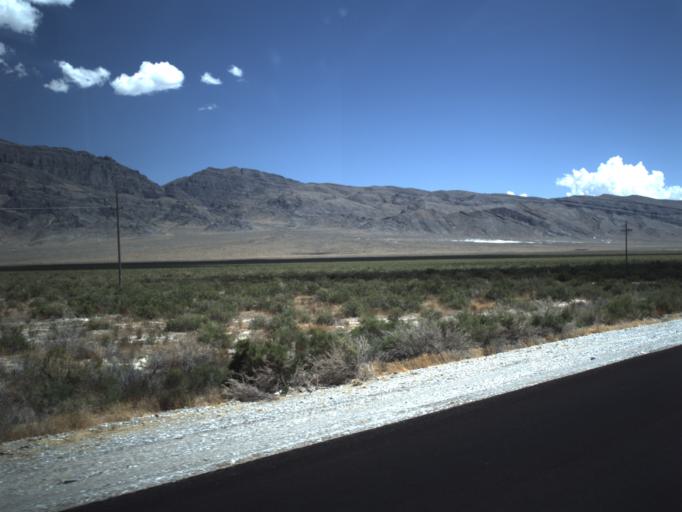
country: US
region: Utah
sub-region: Beaver County
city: Milford
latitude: 39.0805
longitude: -113.4881
